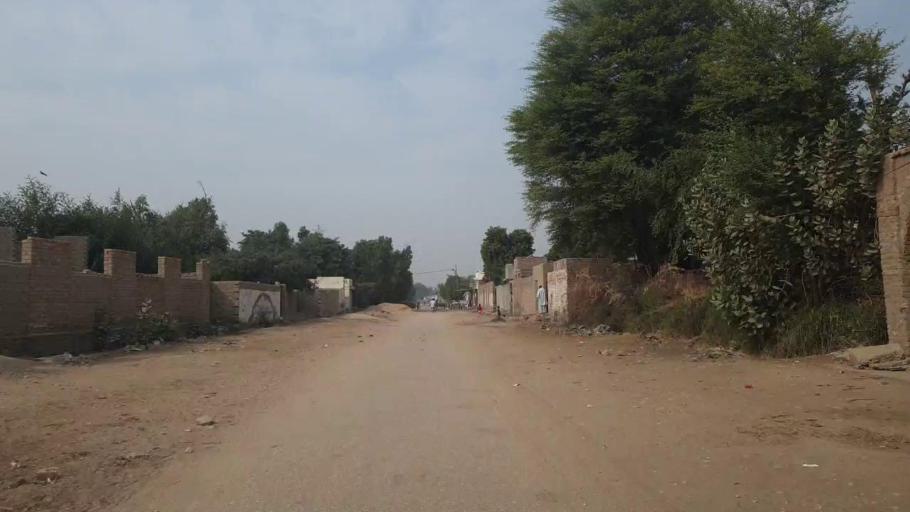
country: PK
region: Sindh
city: Sann
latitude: 26.0368
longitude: 68.1401
